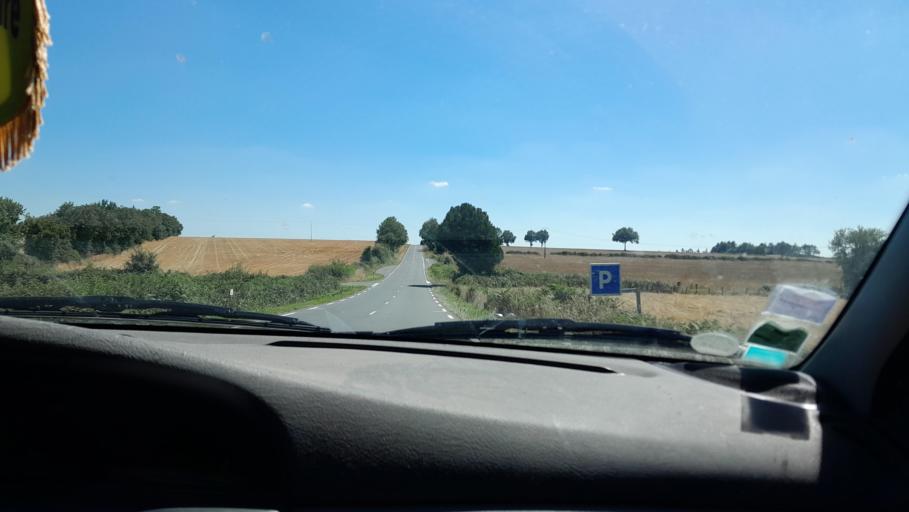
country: FR
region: Pays de la Loire
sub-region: Departement de la Loire-Atlantique
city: Saint-Mars-la-Jaille
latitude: 47.5410
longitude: -1.1866
